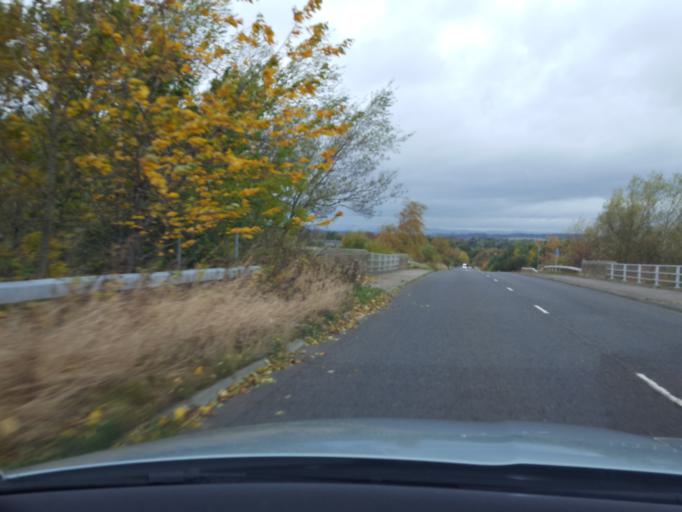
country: GB
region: Scotland
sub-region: Edinburgh
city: Currie
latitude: 55.9198
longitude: -3.3151
